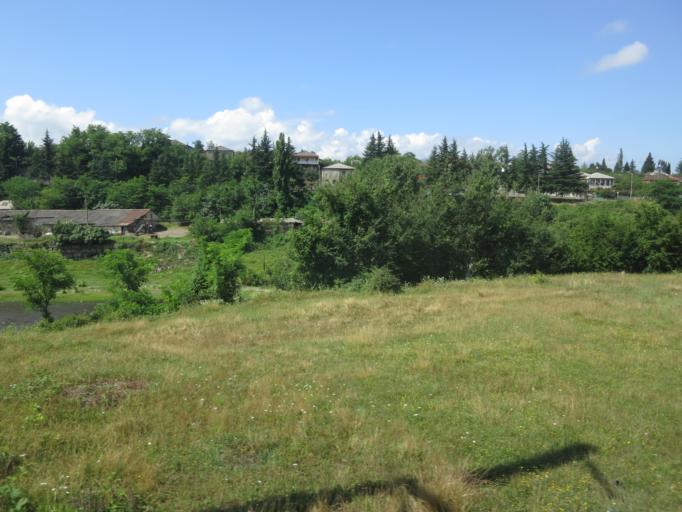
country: GE
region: Imereti
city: Zestap'oni
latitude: 42.1065
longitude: 43.0543
